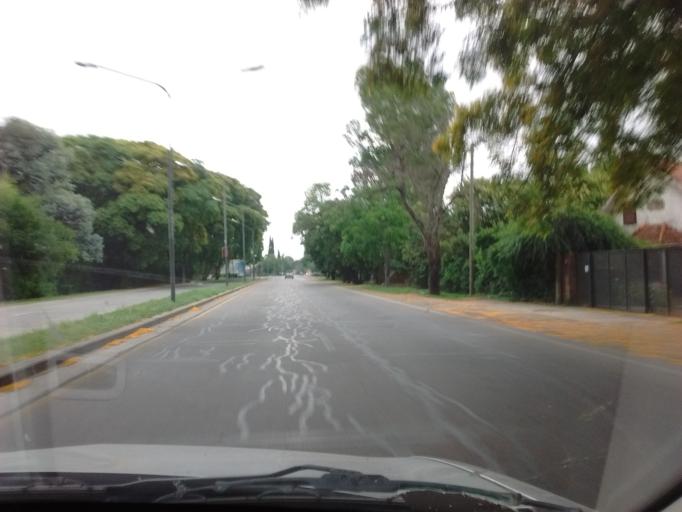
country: AR
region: Santa Fe
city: Funes
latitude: -32.9269
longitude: -60.7460
